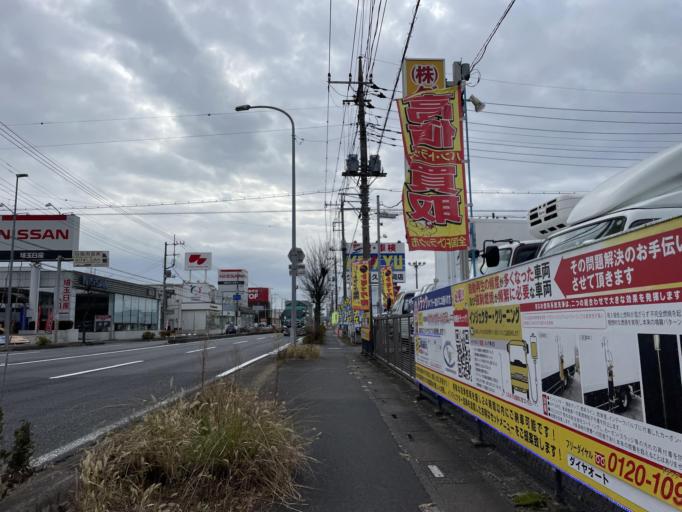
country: JP
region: Saitama
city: Shiraoka
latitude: 36.0256
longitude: 139.6522
